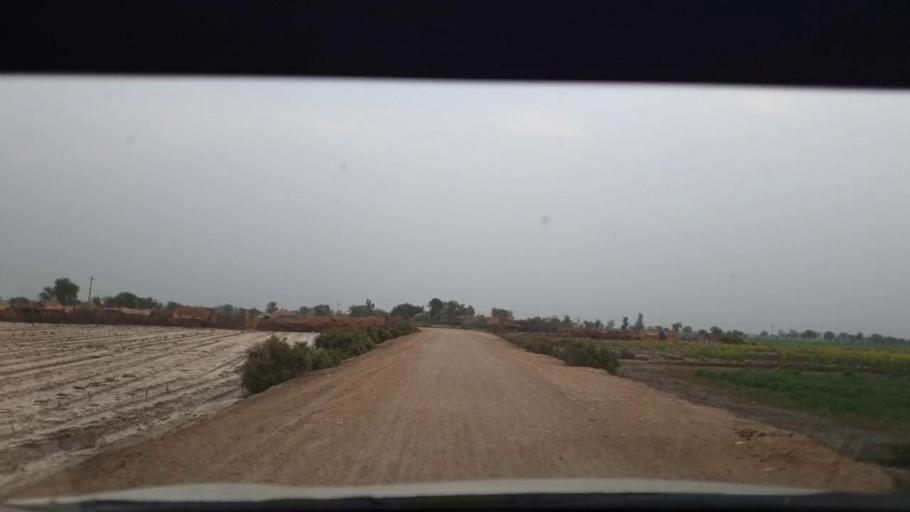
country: PK
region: Sindh
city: Berani
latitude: 25.8702
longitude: 68.7595
